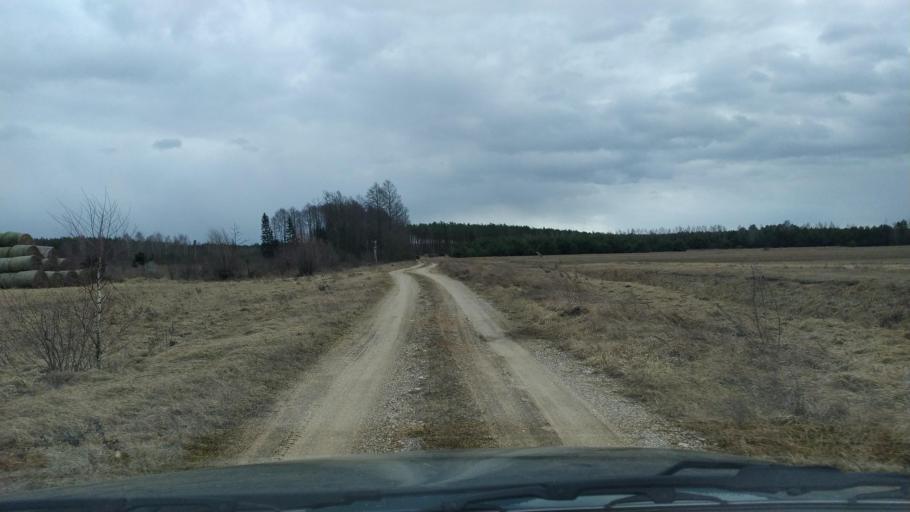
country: BY
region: Brest
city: Zhabinka
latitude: 52.4069
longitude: 24.0687
